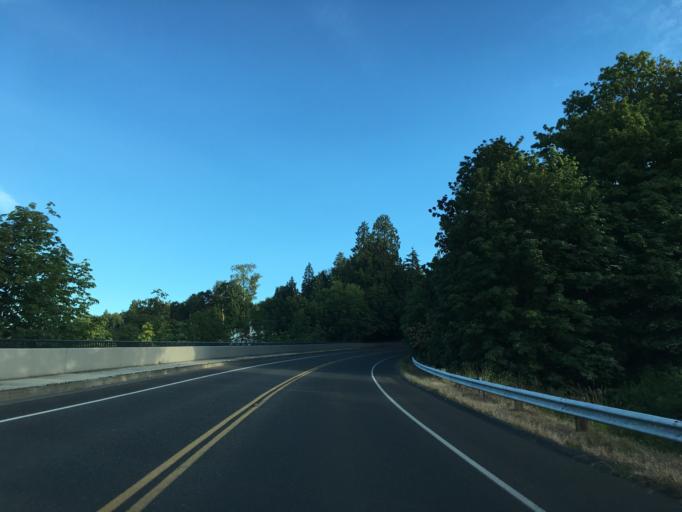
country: CA
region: British Columbia
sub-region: Greater Vancouver Regional District
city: White Rock
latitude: 48.9777
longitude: -122.7911
